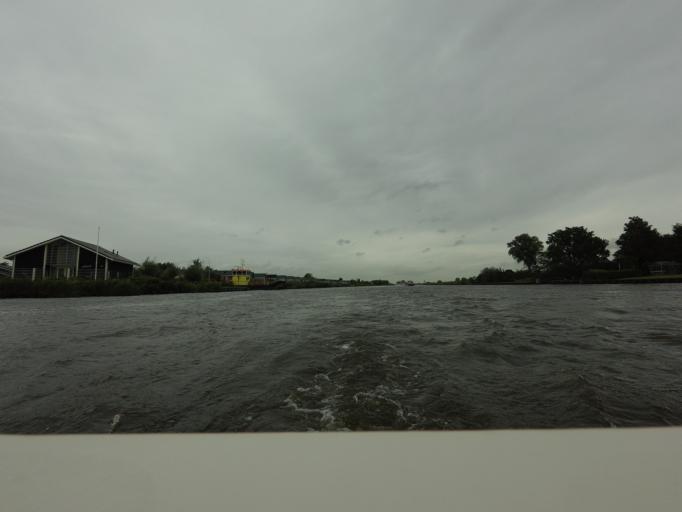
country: NL
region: Friesland
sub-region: Gemeente Boarnsterhim
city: Grou
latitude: 53.1000
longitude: 5.8495
